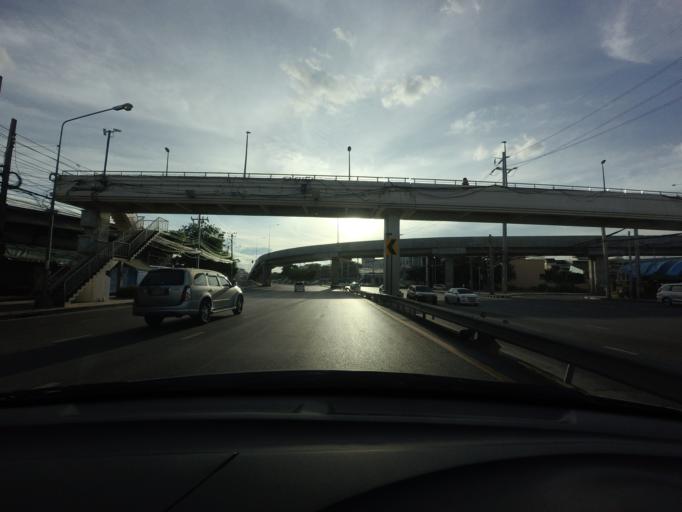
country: TH
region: Nonthaburi
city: Bang Kruai
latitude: 13.7900
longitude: 100.4775
